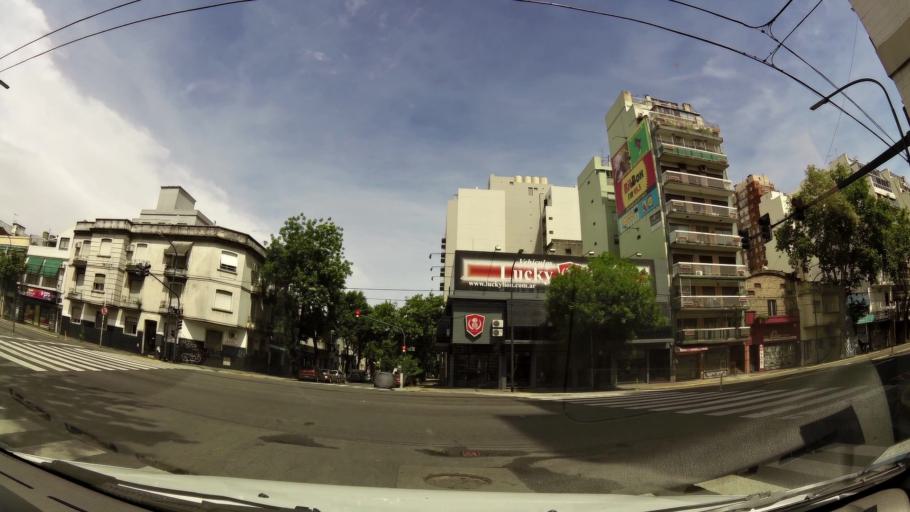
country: AR
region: Buenos Aires F.D.
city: Villa Santa Rita
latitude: -34.6027
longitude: -58.4561
